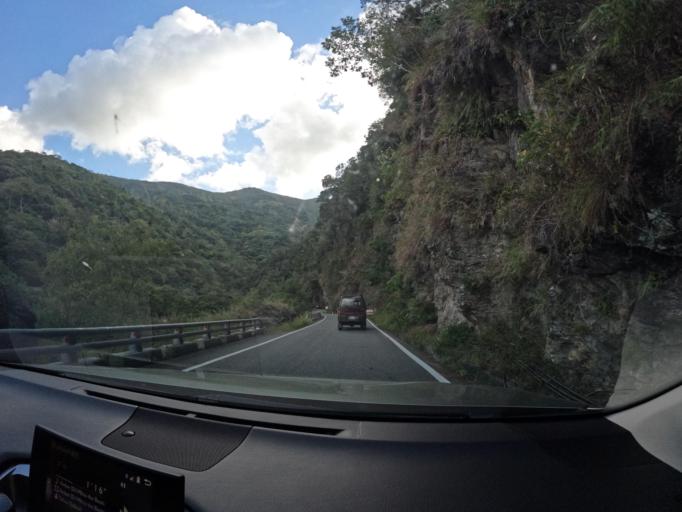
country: TW
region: Taiwan
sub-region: Taitung
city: Taitung
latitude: 23.1613
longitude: 121.0505
